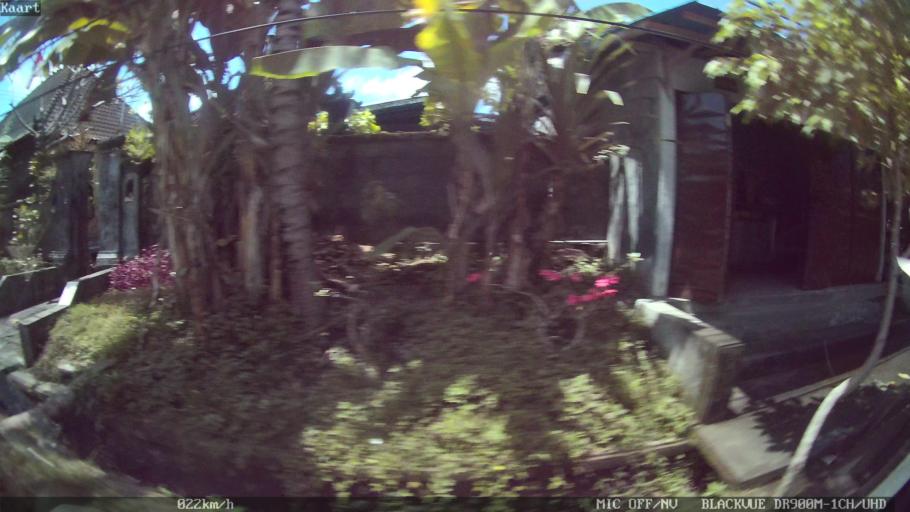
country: ID
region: Bali
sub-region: Kabupaten Gianyar
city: Ubud
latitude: -8.5582
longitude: 115.3167
